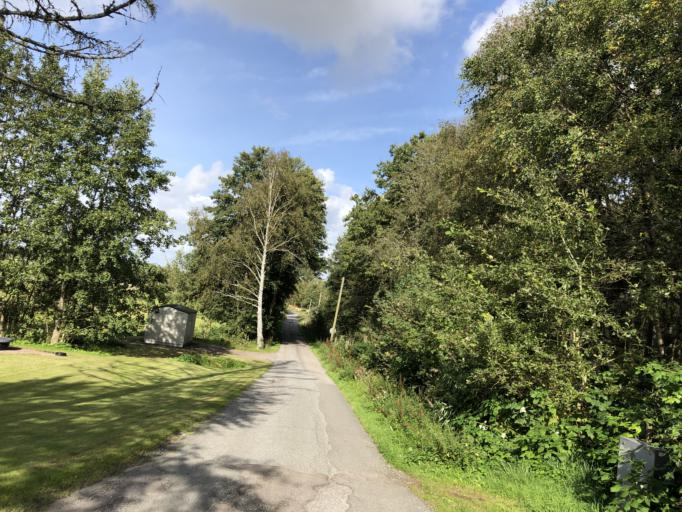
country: SE
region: Vaestra Goetaland
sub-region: Goteborg
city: Majorna
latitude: 57.7492
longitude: 11.8612
